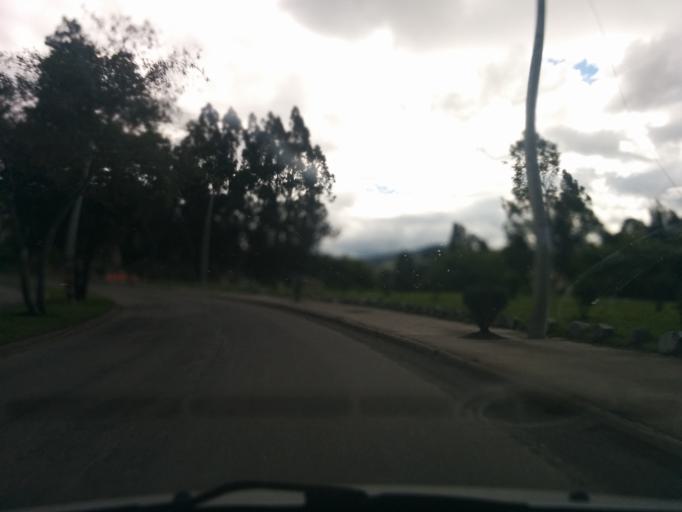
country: EC
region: Azuay
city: Cuenca
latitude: -2.9203
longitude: -79.0275
